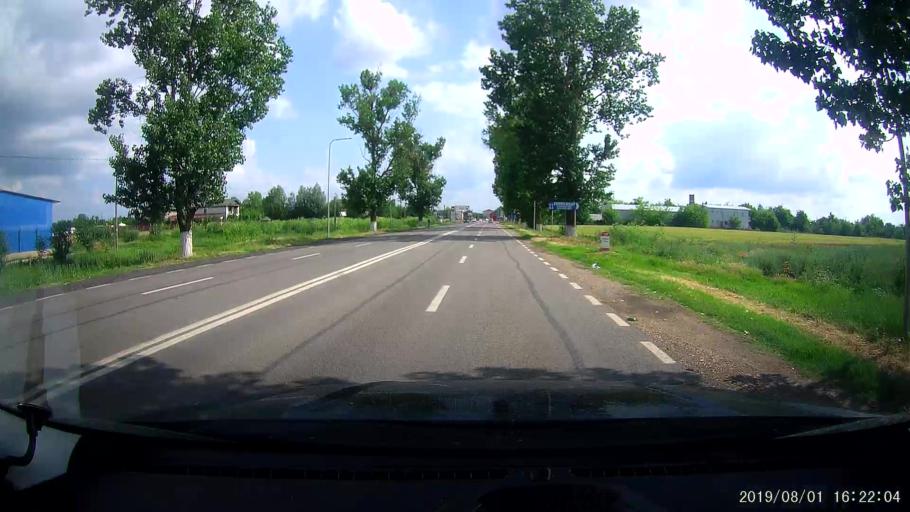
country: RO
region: Calarasi
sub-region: Municipiul Calarasi
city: Calarasi
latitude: 44.2080
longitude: 27.3383
